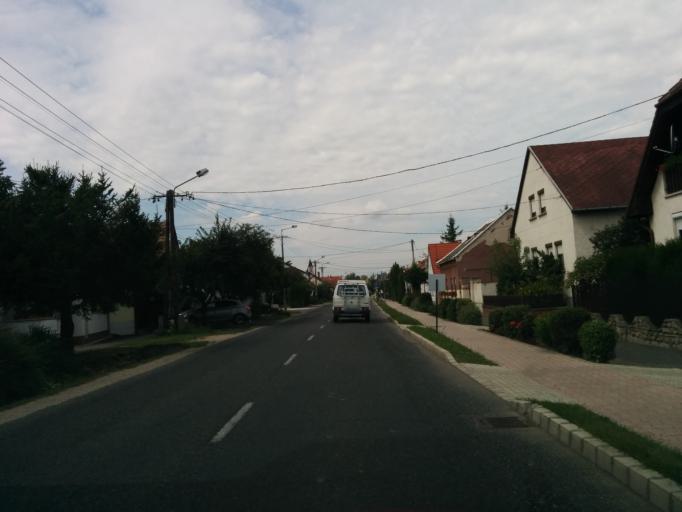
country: HU
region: Gyor-Moson-Sopron
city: Nagycenk
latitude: 47.6211
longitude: 16.7721
